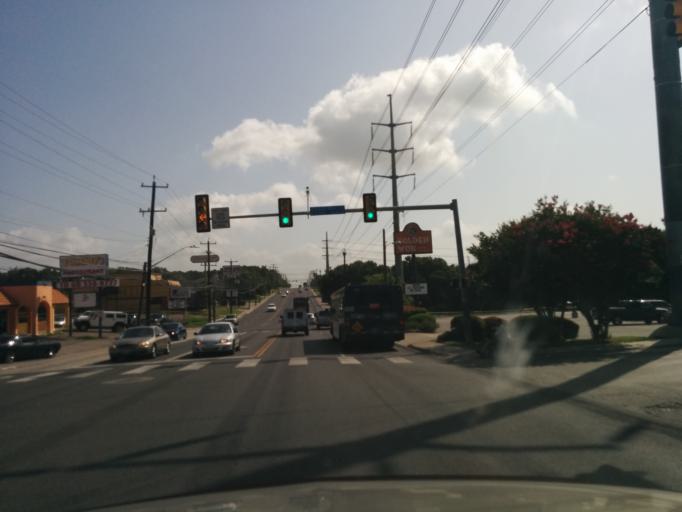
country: US
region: Texas
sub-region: Bexar County
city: Balcones Heights
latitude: 29.5246
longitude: -98.5689
